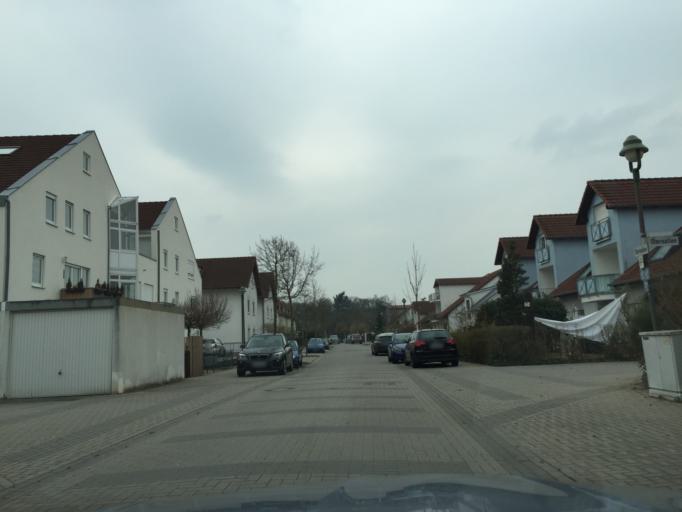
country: DE
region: Baden-Wuerttemberg
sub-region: Karlsruhe Region
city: Schwetzingen
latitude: 49.3785
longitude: 8.5642
